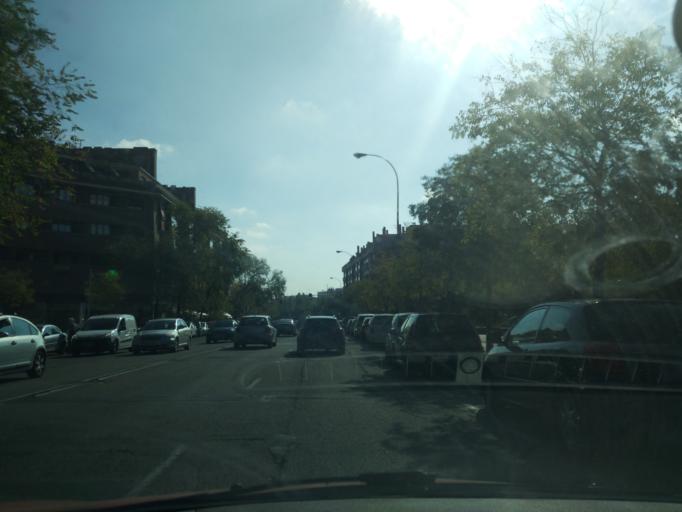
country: ES
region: Madrid
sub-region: Provincia de Madrid
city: Fuencarral-El Pardo
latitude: 40.4879
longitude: -3.7165
